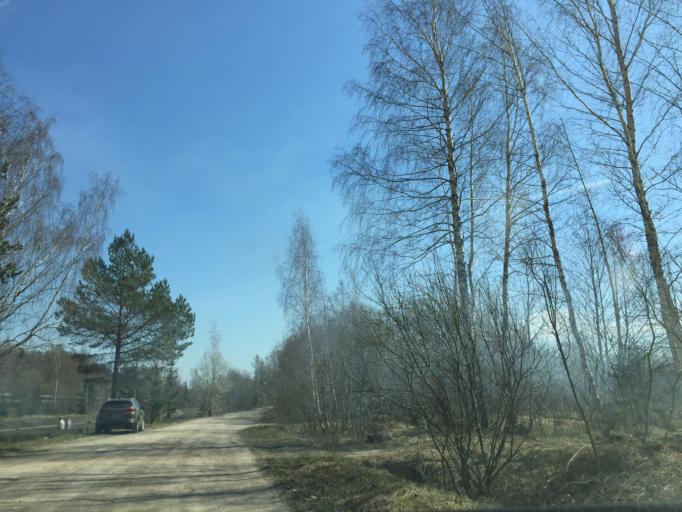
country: EE
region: Ida-Virumaa
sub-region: Narva linn
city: Narva
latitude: 59.3535
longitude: 28.1430
